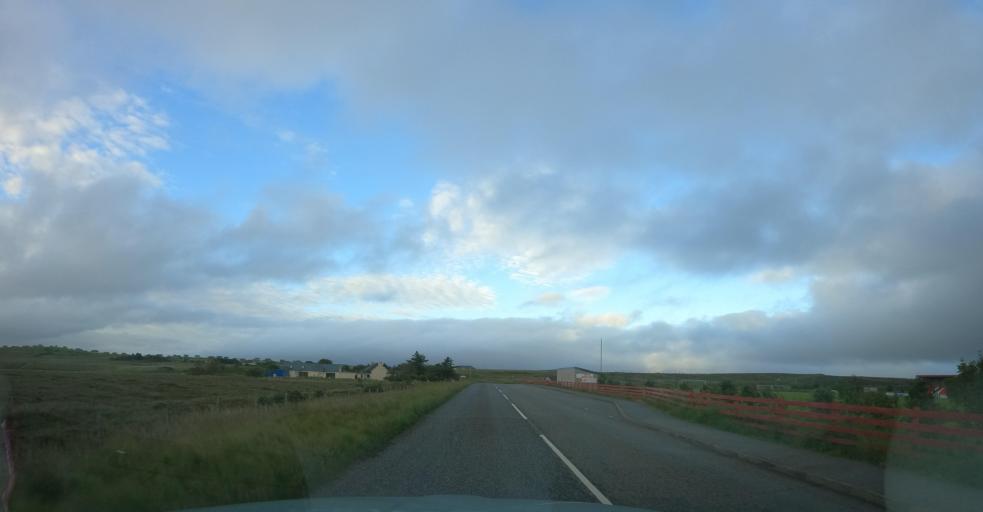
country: GB
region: Scotland
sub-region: Eilean Siar
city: Stornoway
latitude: 58.2090
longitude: -6.2560
